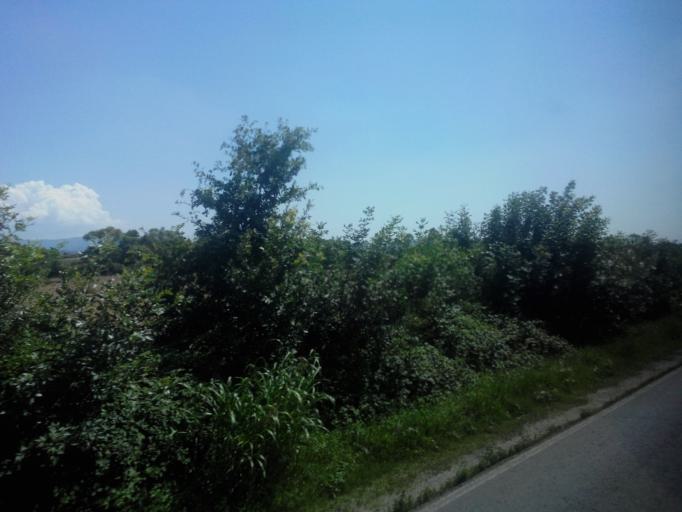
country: RO
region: Timis
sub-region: Comuna Faget
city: Faget
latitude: 45.8428
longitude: 22.1479
